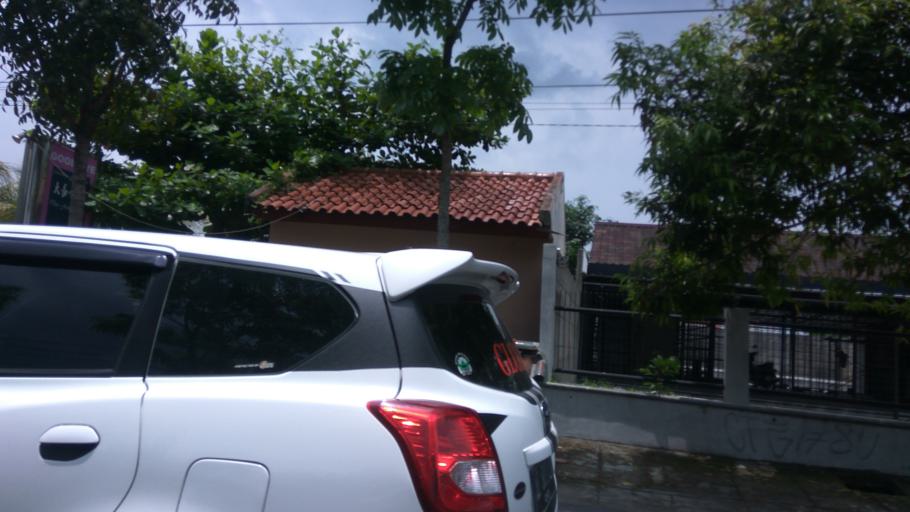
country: ID
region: Daerah Istimewa Yogyakarta
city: Melati
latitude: -7.7269
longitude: 110.3805
